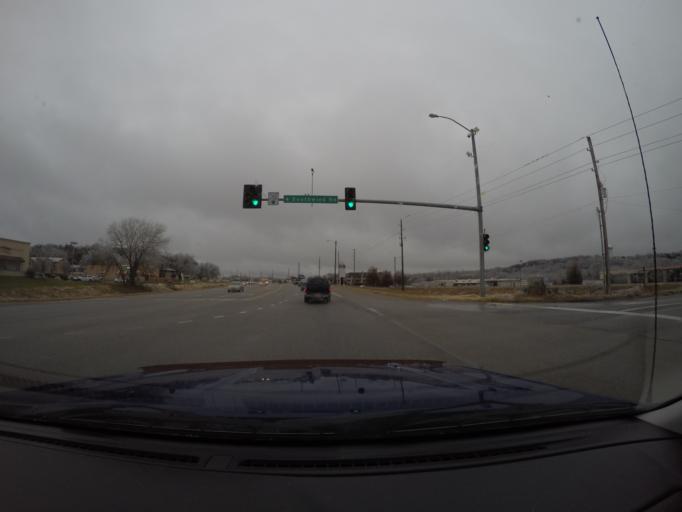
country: US
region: Kansas
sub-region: Riley County
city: Manhattan
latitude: 39.1734
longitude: -96.6036
